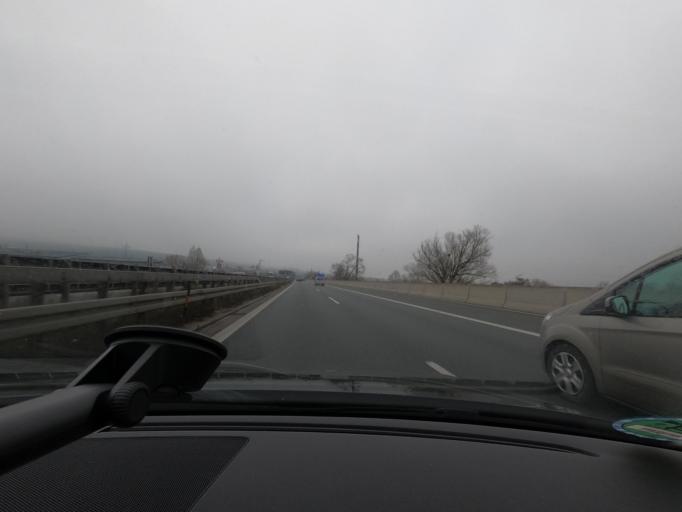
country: DE
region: Bavaria
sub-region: Regierungsbezirk Mittelfranken
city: Mohrendorf
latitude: 49.6320
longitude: 11.0089
